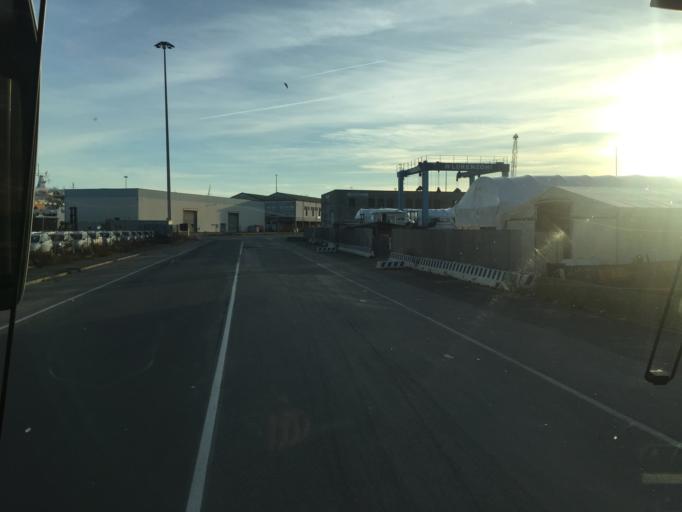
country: IT
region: Tuscany
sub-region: Provincia di Livorno
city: Livorno
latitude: 43.5595
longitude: 10.3027
